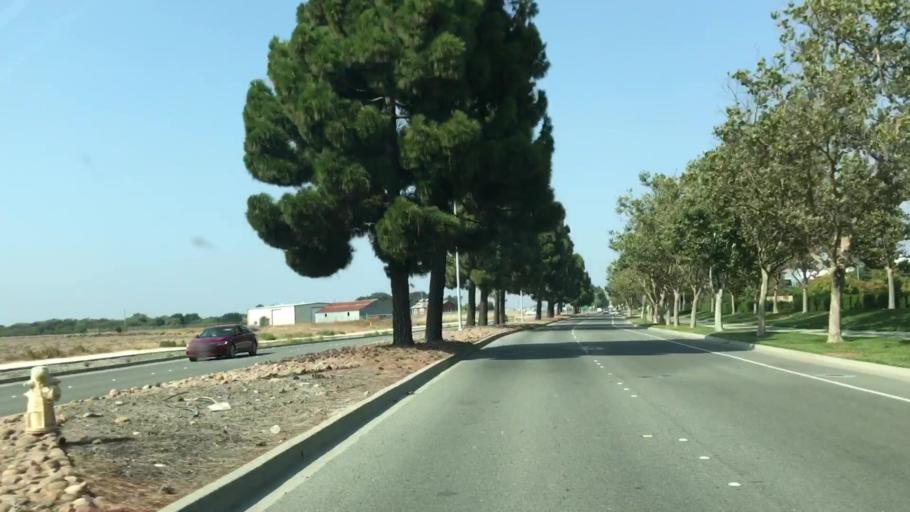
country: US
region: California
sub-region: Alameda County
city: Newark
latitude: 37.5518
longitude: -122.0692
